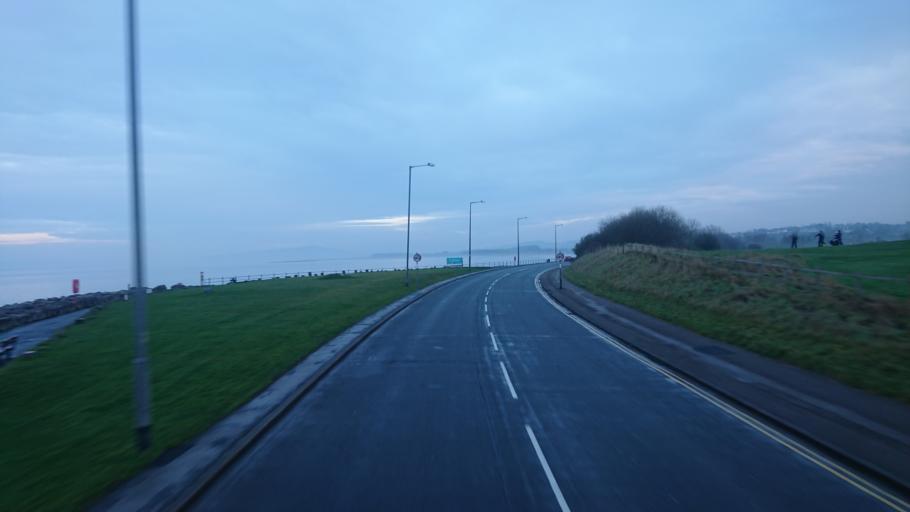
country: GB
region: England
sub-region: Lancashire
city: Morecambe
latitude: 54.0839
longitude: -2.8332
